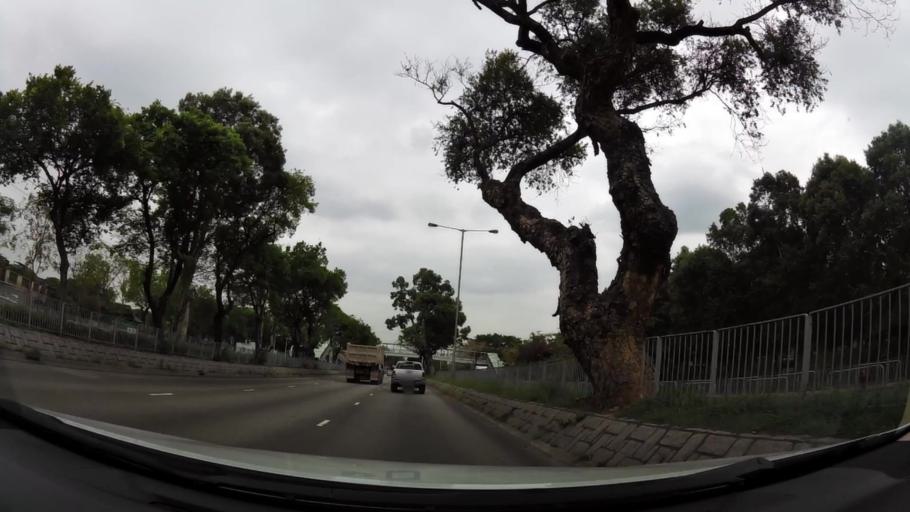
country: HK
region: Tuen Mun
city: Tuen Mun
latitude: 22.4230
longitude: 113.9860
